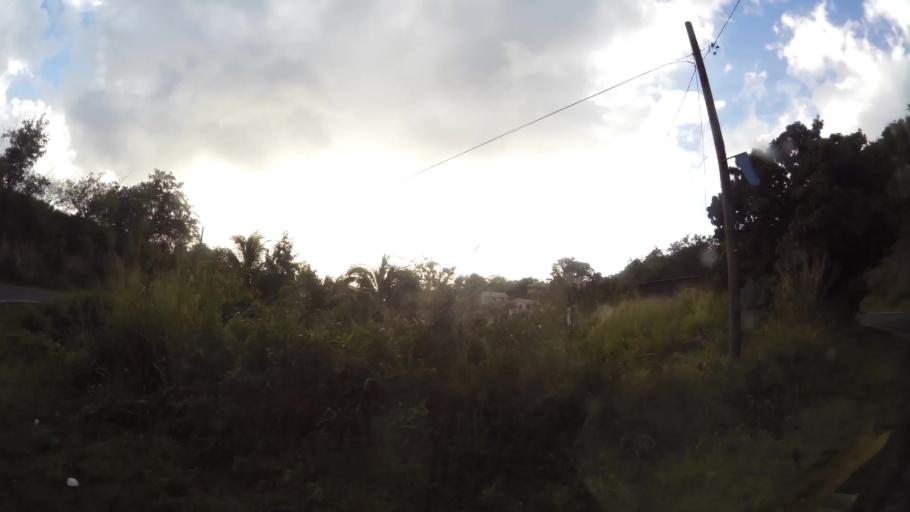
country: DM
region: Saint Joseph
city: Saint Joseph
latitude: 15.3989
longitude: -61.4238
